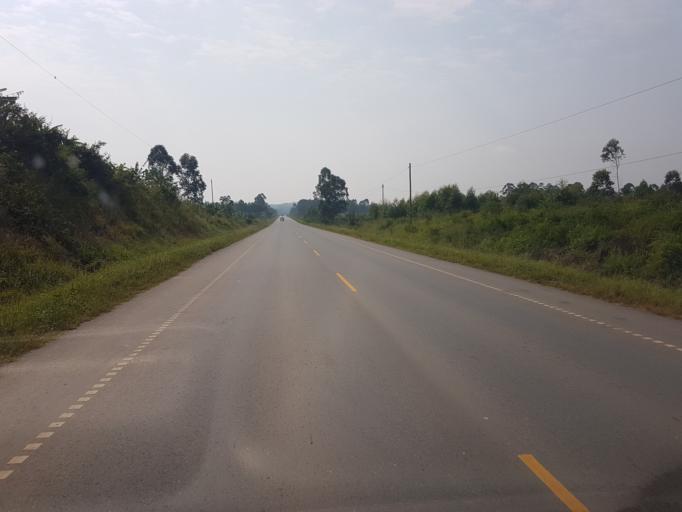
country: UG
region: Western Region
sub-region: Mbarara District
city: Bwizibwera
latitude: -0.6427
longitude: 30.5654
